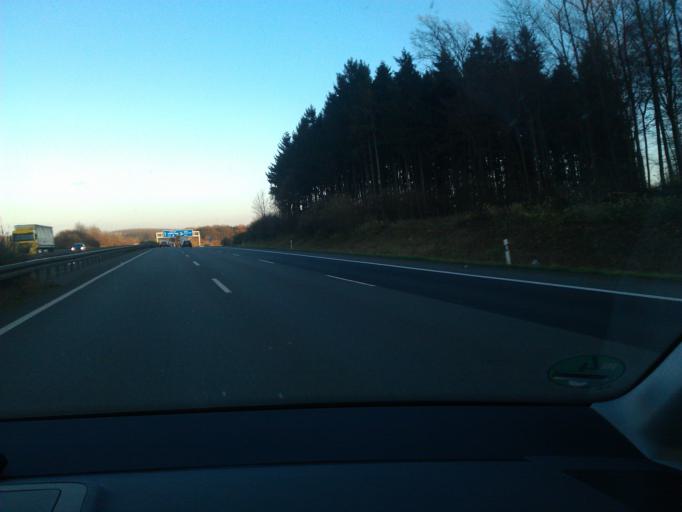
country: DE
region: North Rhine-Westphalia
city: Oelde
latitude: 51.8041
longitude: 8.1165
